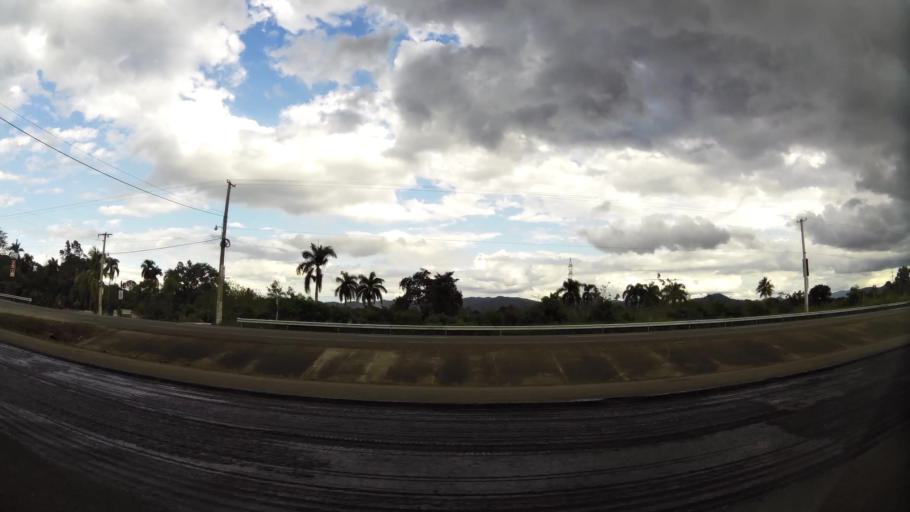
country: DO
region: Monsenor Nouel
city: Sabana del Puerto
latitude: 19.0603
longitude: -70.4463
